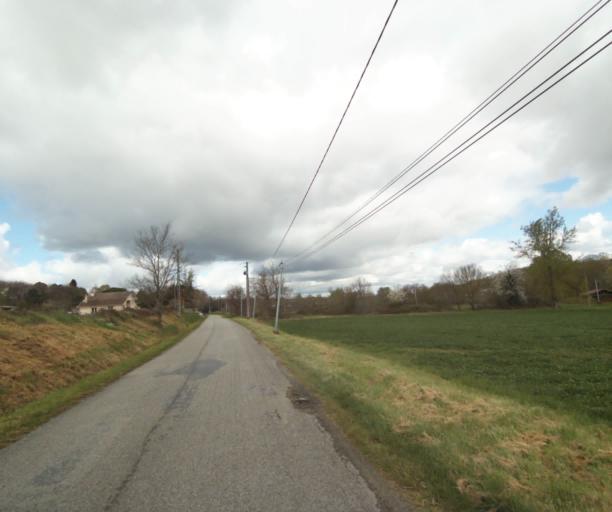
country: FR
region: Midi-Pyrenees
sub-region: Departement de l'Ariege
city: Saverdun
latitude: 43.2165
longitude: 1.5744
